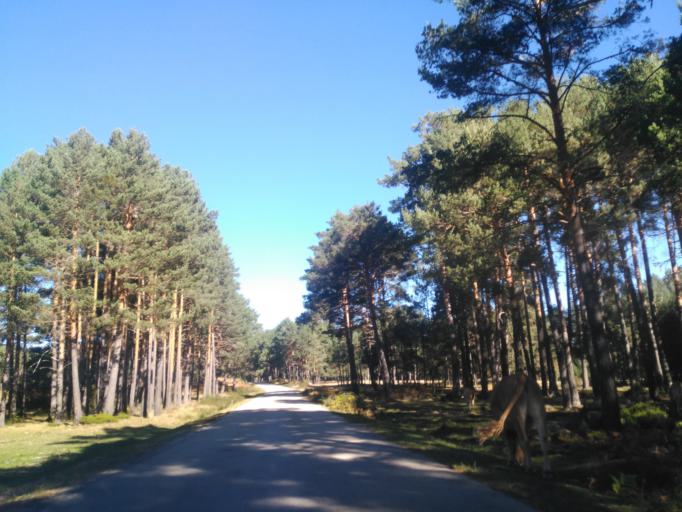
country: ES
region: Castille and Leon
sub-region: Provincia de Soria
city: Vinuesa
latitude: 41.9827
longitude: -2.7968
